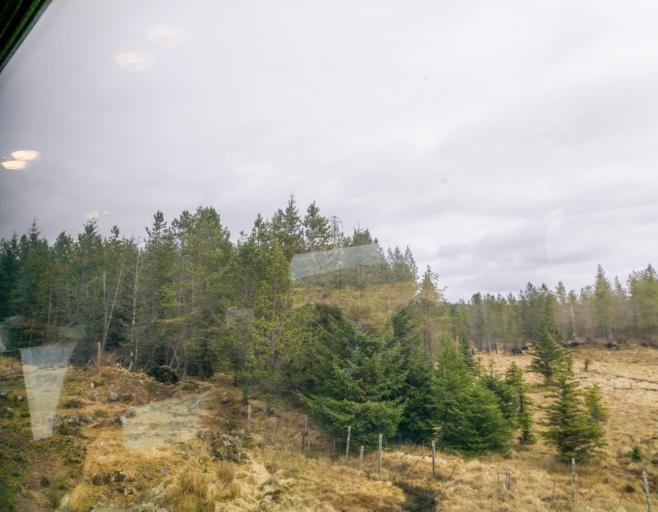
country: GB
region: Scotland
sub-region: Highland
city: Spean Bridge
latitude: 56.6534
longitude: -4.5659
